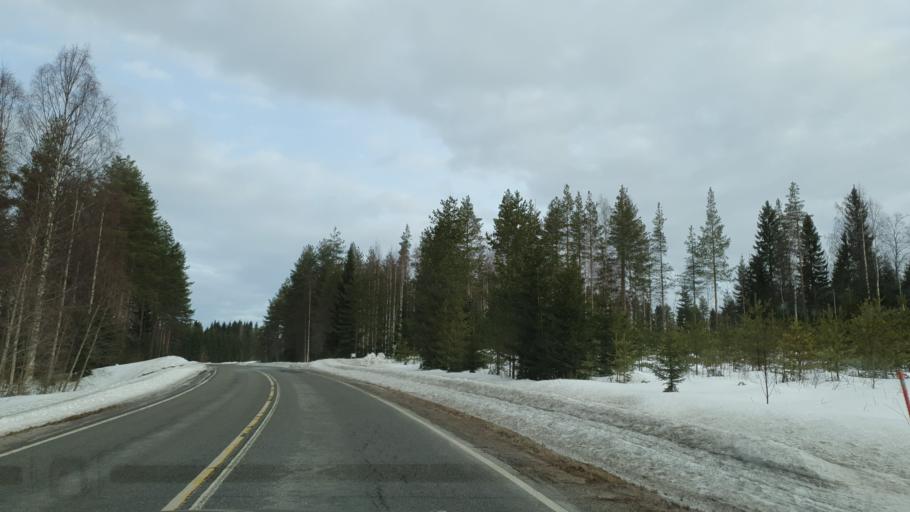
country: FI
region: Kainuu
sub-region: Kajaani
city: Vuokatti
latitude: 64.2443
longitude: 28.0558
